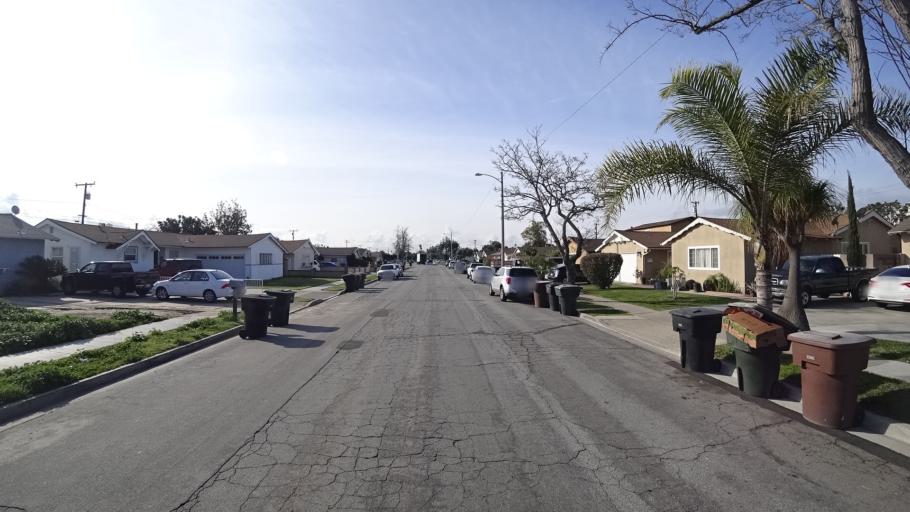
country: US
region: California
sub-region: Orange County
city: Stanton
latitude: 33.8227
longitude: -117.9694
